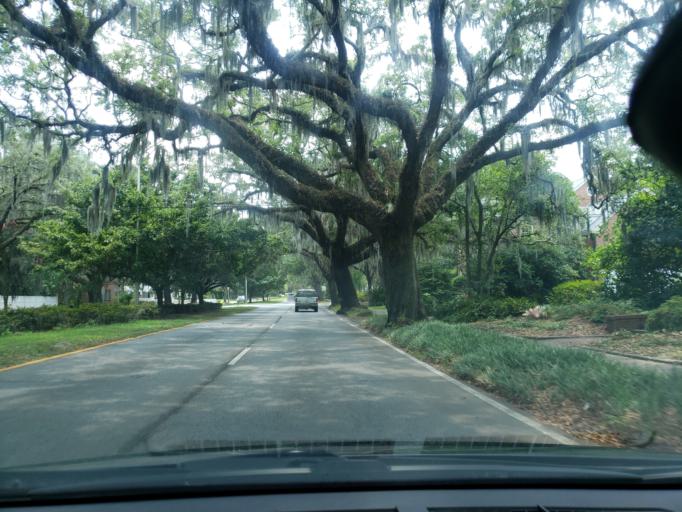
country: US
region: Georgia
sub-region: Chatham County
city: Savannah
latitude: 32.0453
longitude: -81.1022
